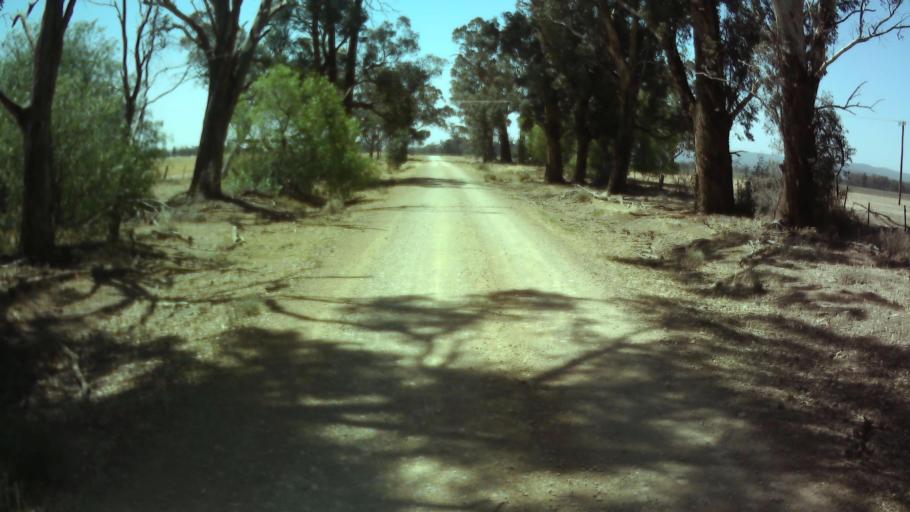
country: AU
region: New South Wales
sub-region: Weddin
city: Grenfell
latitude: -34.0288
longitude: 147.8996
